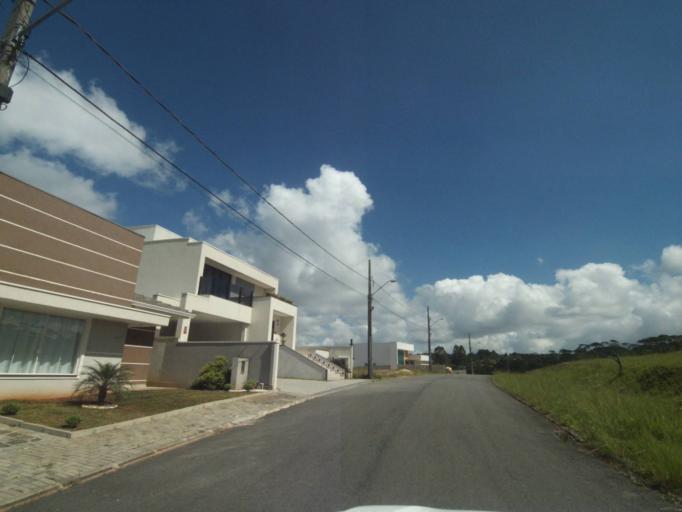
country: BR
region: Parana
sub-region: Colombo
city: Colombo
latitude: -25.3108
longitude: -49.2334
